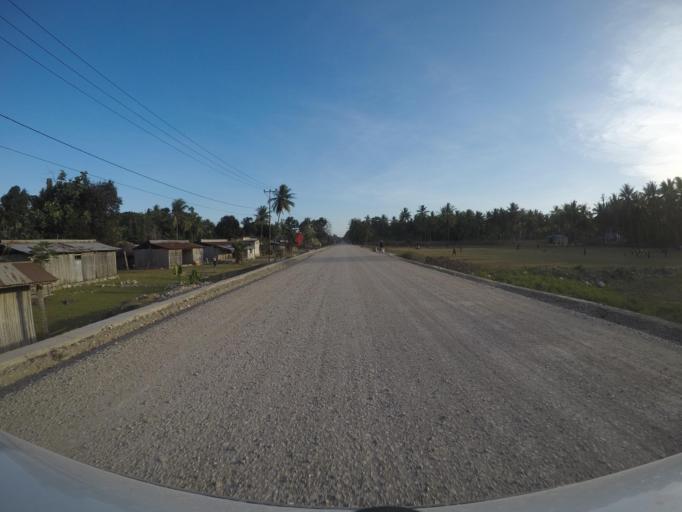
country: TL
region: Viqueque
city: Viqueque
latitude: -8.8500
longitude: 126.5128
